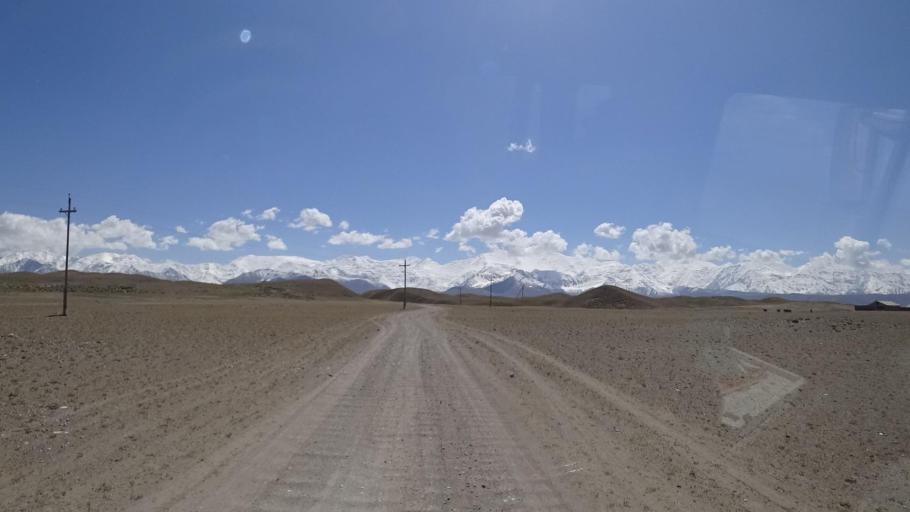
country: KG
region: Osh
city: Gul'cha
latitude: 39.6123
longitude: 72.8749
